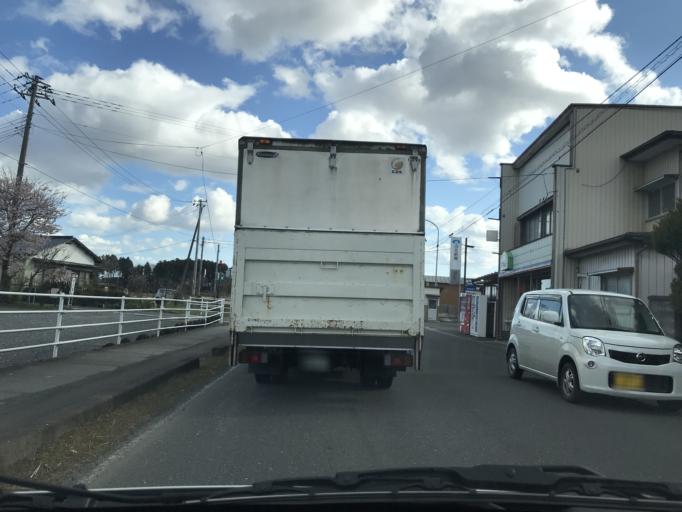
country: JP
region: Miyagi
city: Wakuya
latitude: 38.6610
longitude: 141.1932
